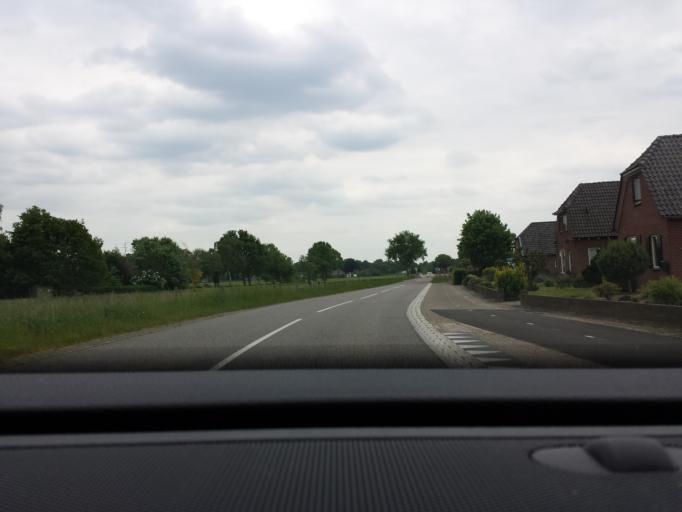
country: NL
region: Gelderland
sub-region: Gemeente Bronckhorst
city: Zelhem
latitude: 52.0187
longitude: 6.3385
